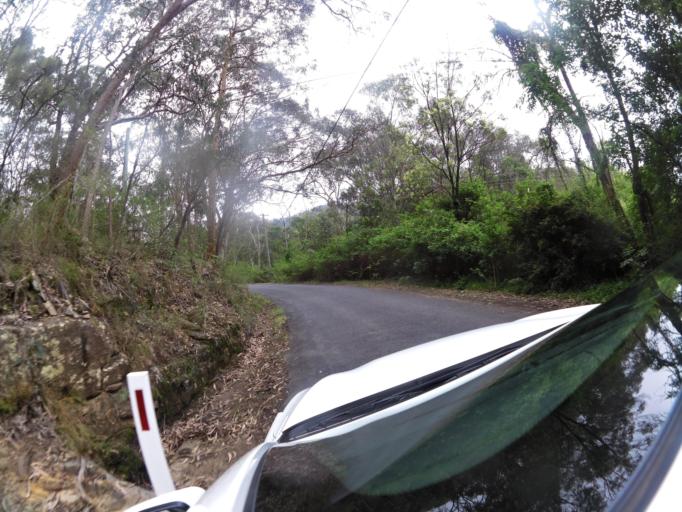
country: AU
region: New South Wales
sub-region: Hornsby Shire
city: Glenorie
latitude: -33.4160
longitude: 150.9567
